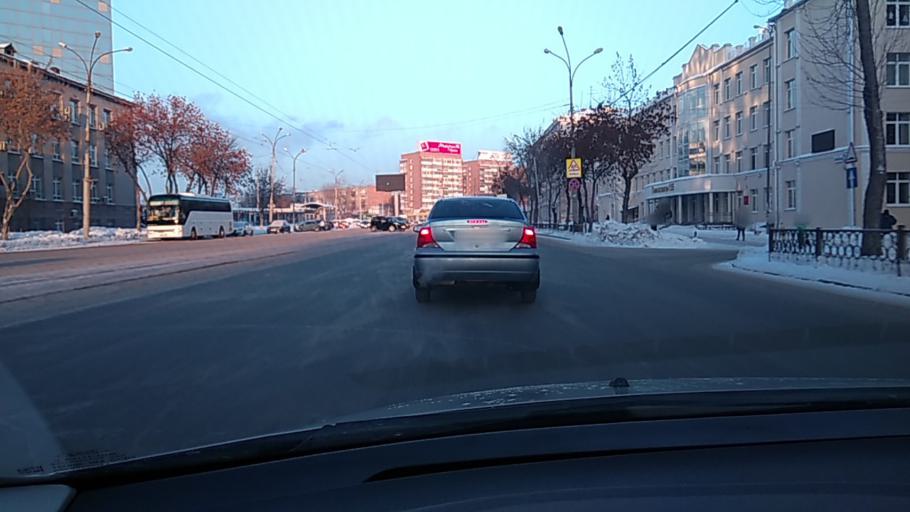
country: RU
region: Sverdlovsk
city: Yekaterinburg
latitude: 56.8542
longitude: 60.5986
